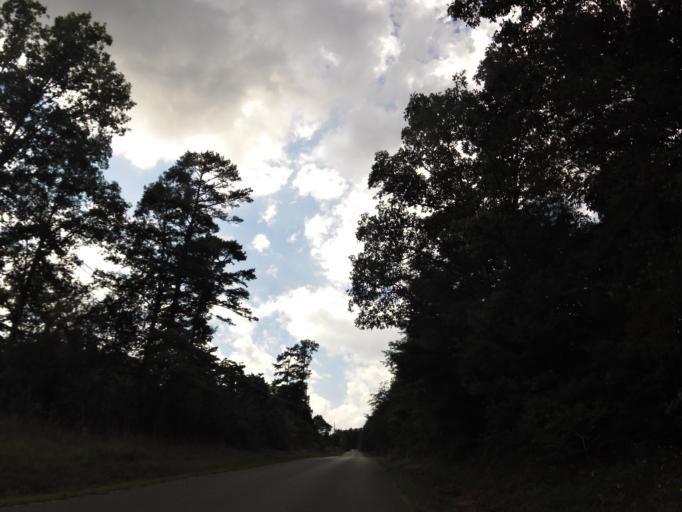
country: US
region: Tennessee
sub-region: Roane County
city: Rockwood
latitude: 35.8903
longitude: -84.7917
